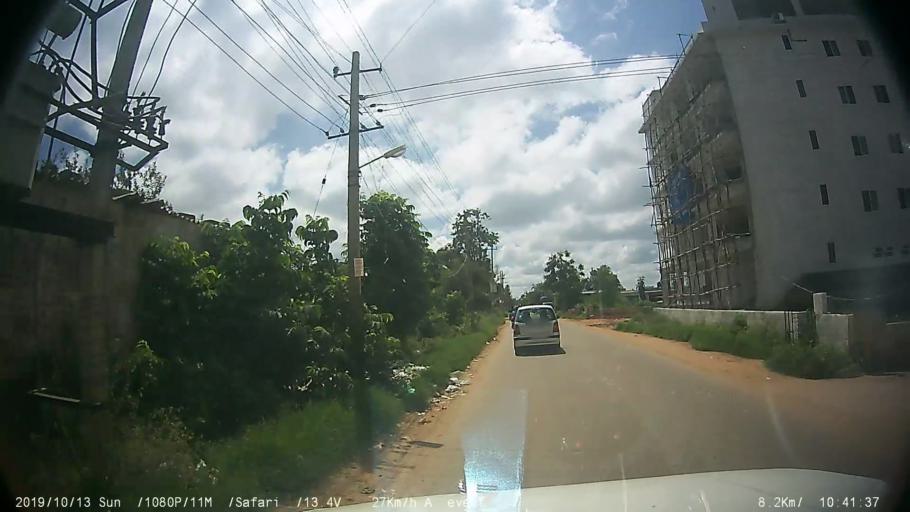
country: IN
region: Karnataka
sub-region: Bangalore Urban
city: Anekal
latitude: 12.8257
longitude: 77.6499
